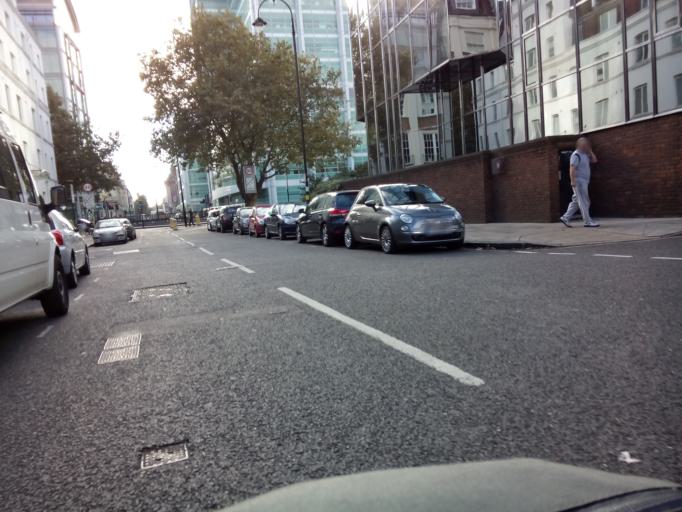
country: GB
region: England
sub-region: Greater London
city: Camden Town
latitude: 51.5263
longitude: -0.1365
